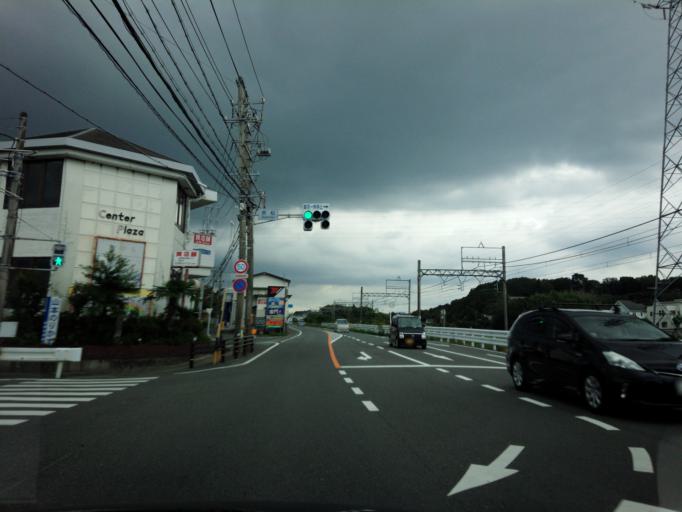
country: JP
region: Mie
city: Toba
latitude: 34.3383
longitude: 136.8172
